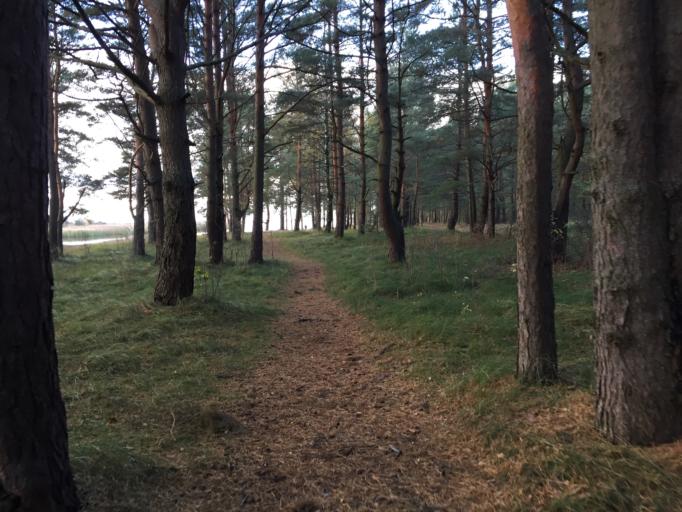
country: LV
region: Carnikava
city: Carnikava
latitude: 57.1553
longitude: 24.2756
